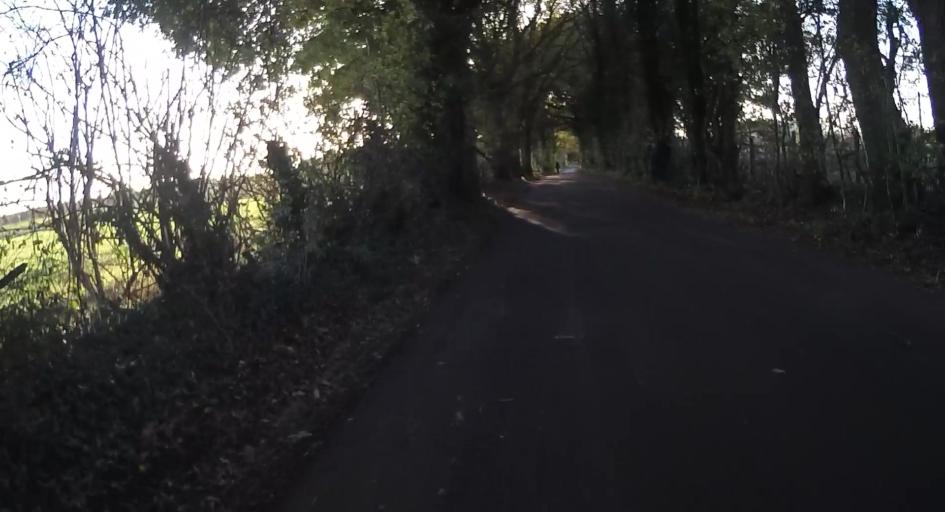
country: GB
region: England
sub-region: Wokingham
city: Wokingham
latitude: 51.4017
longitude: -0.8183
